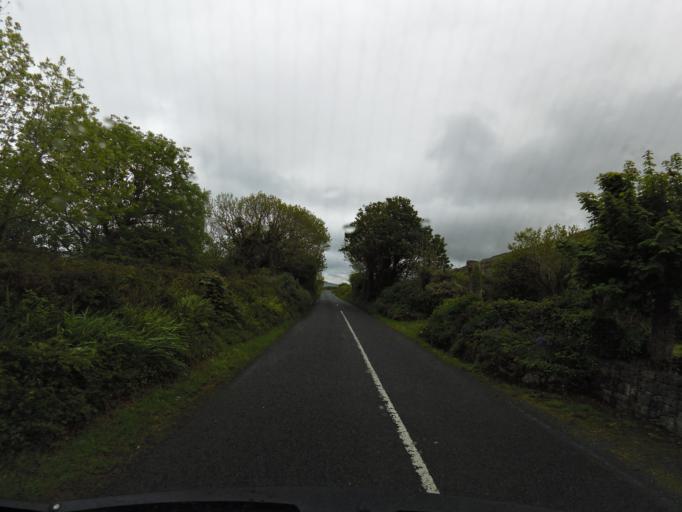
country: IE
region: Connaught
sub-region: County Galway
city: Bearna
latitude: 53.1337
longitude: -9.1965
